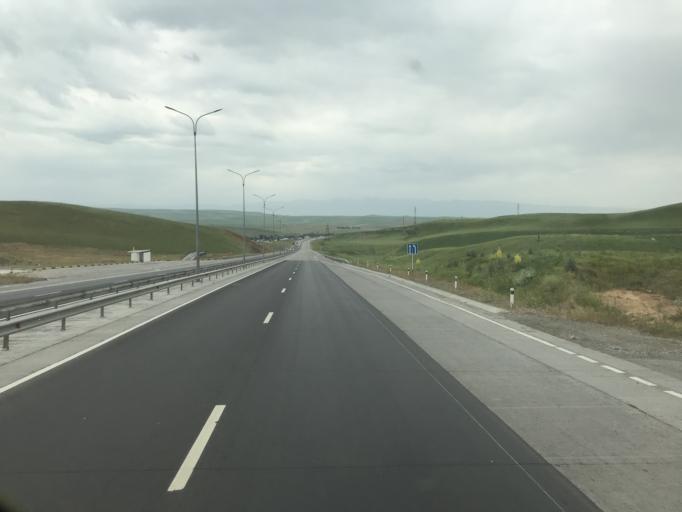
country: KZ
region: Ongtustik Qazaqstan
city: Qazyqurt
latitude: 41.9937
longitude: 69.4801
